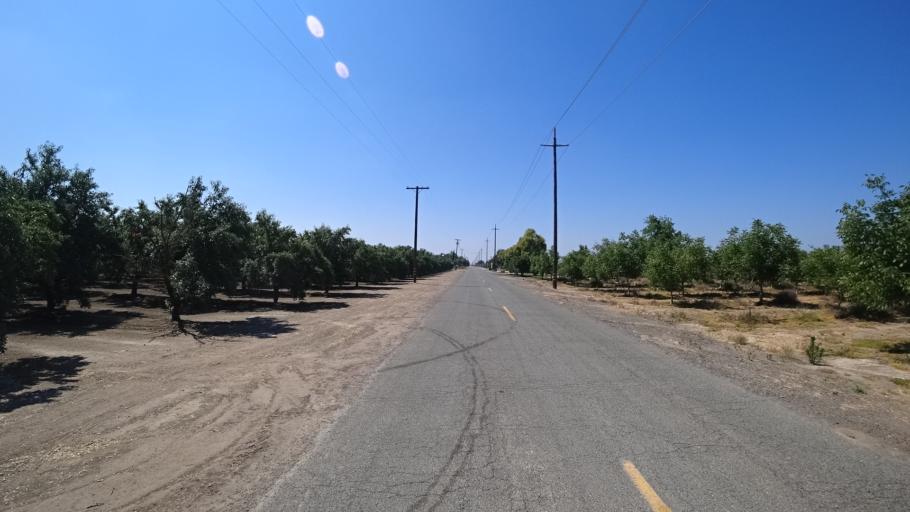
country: US
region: California
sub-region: Fresno County
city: Kingsburg
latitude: 36.4503
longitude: -119.5825
